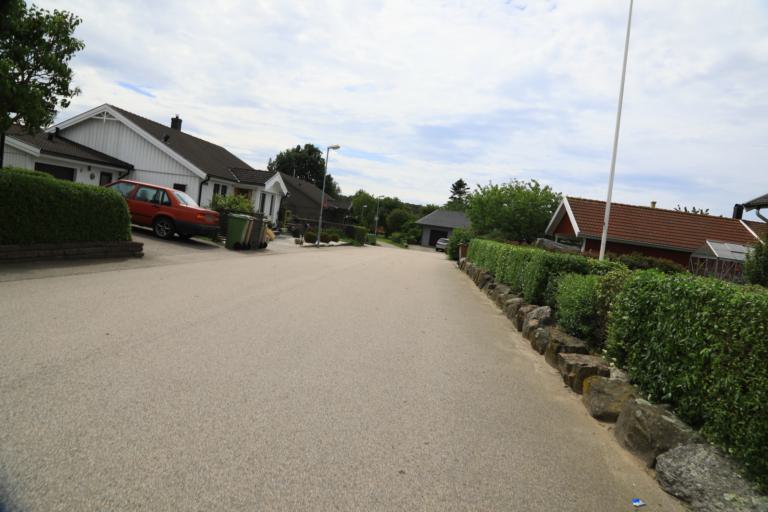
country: SE
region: Halland
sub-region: Varbergs Kommun
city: Varberg
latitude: 57.1266
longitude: 12.2745
